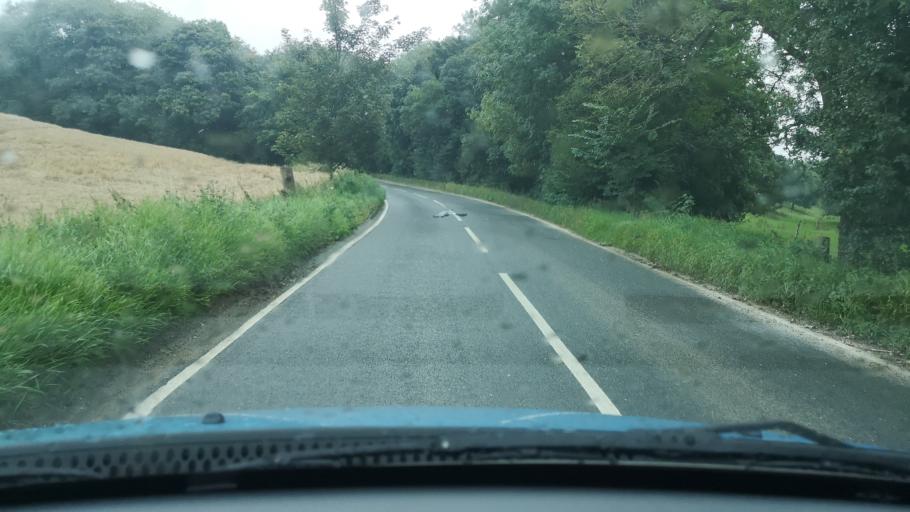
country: GB
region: England
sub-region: City and Borough of Wakefield
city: Darrington
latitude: 53.6791
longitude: -1.2512
